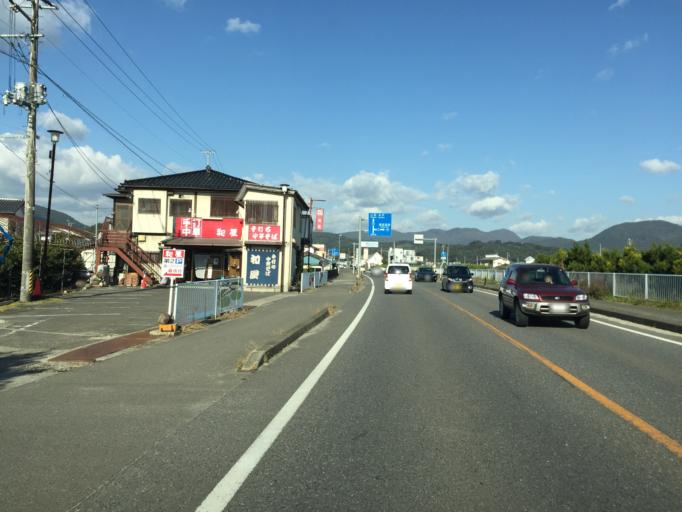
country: JP
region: Fukushima
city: Fukushima-shi
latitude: 37.8137
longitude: 140.4416
